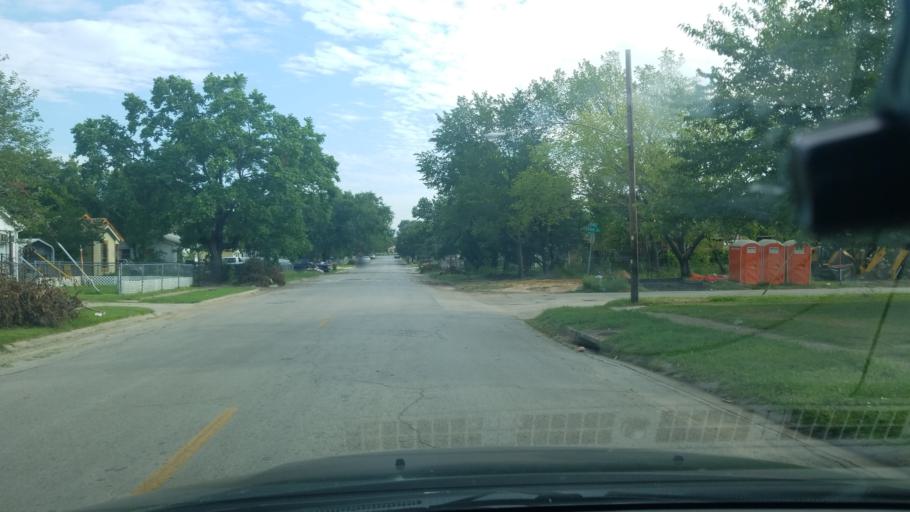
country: US
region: Texas
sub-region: Dallas County
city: Balch Springs
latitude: 32.7394
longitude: -96.6743
